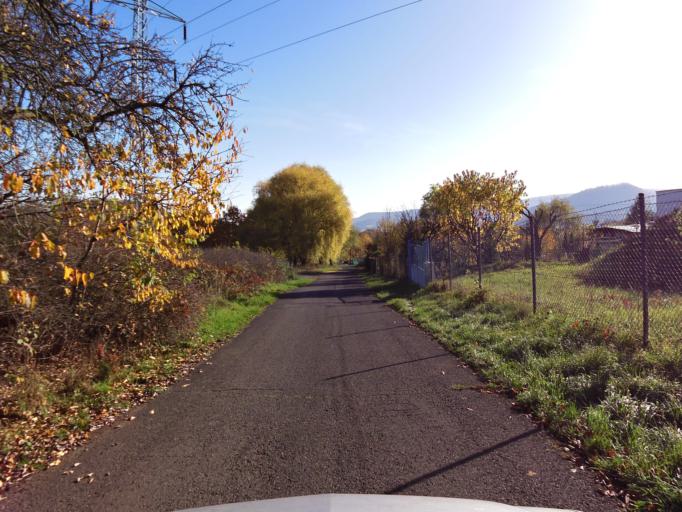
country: CZ
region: Ustecky
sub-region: Okres Chomutov
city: Klasterec nad Ohri
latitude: 50.3898
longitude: 13.1599
